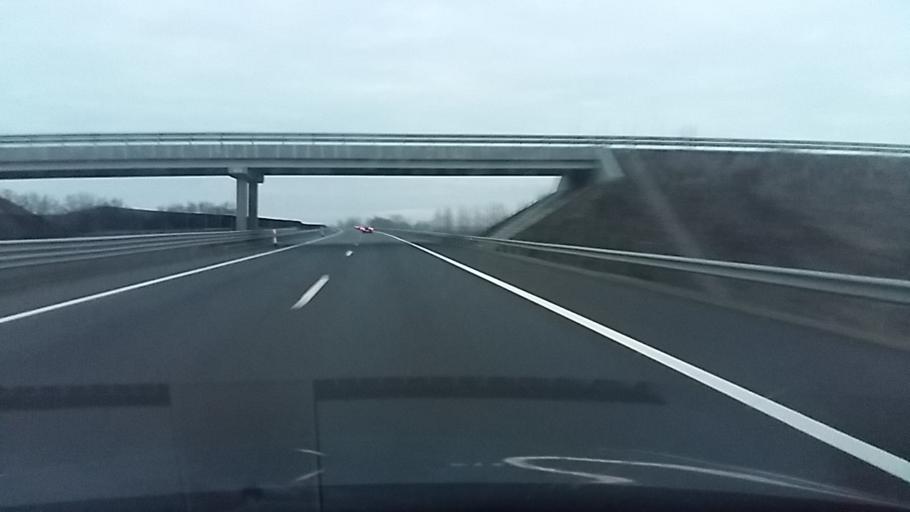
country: HU
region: Hajdu-Bihar
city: Hajduboszormeny
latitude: 47.7089
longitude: 21.4312
